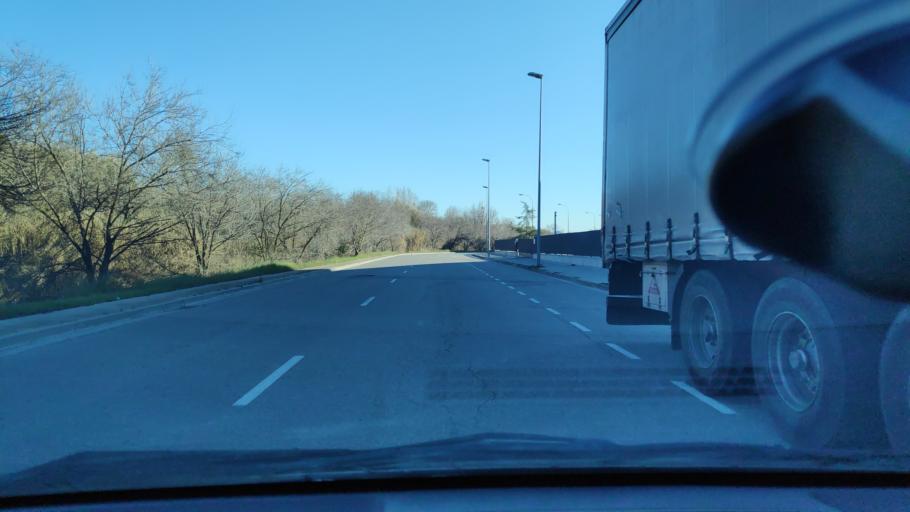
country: ES
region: Catalonia
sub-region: Provincia de Barcelona
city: Sant Quirze del Valles
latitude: 41.5251
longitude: 2.0920
